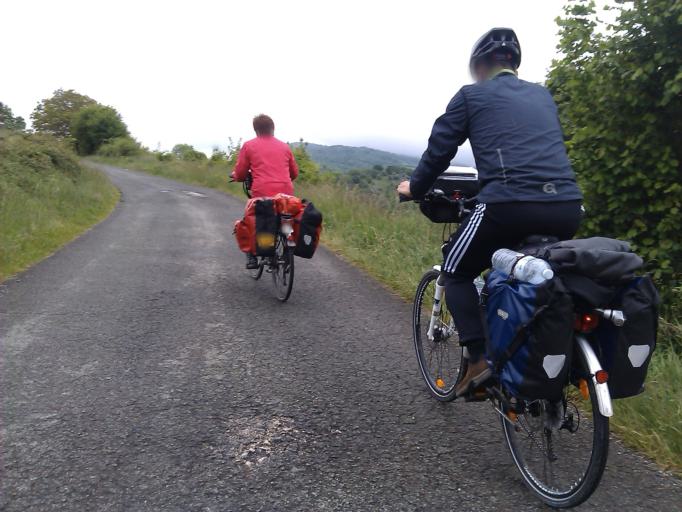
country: ES
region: Navarre
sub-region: Provincia de Navarra
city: Lekunberri
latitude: 42.9950
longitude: -1.8884
